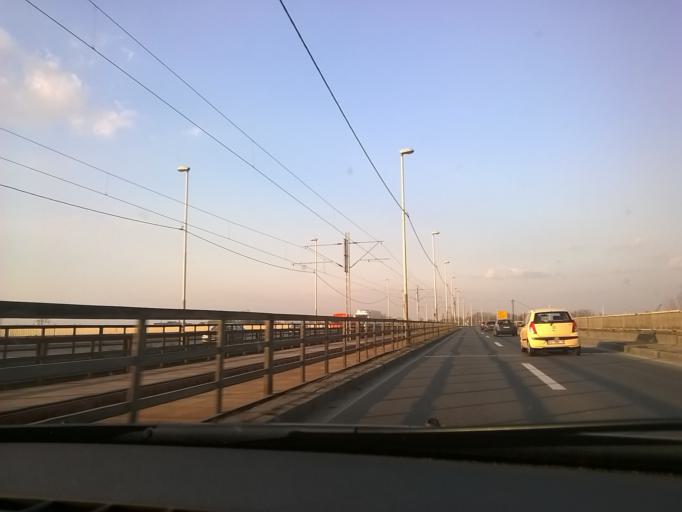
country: RS
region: Central Serbia
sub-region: Belgrade
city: Palilula
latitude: 44.8332
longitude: 20.4930
